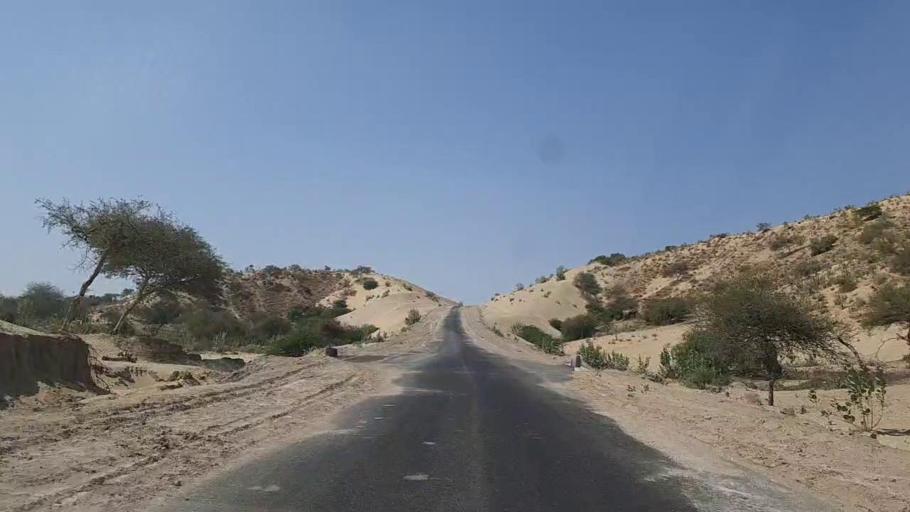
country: PK
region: Sindh
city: Diplo
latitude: 24.5828
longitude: 69.5167
